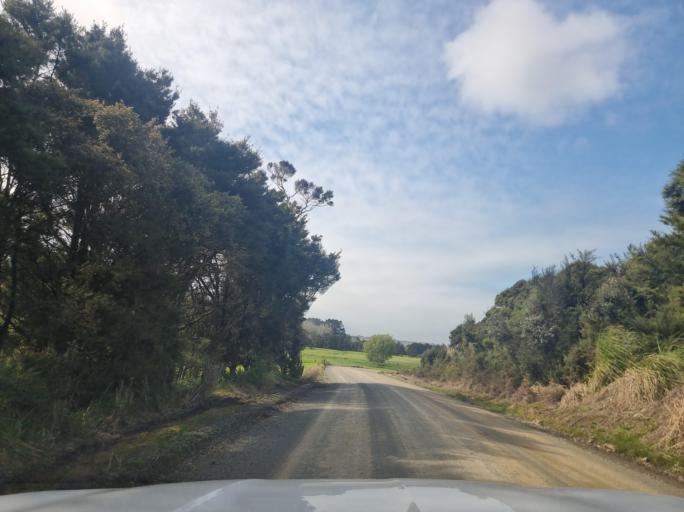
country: NZ
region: Auckland
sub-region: Auckland
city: Wellsford
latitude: -36.1029
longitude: 174.4979
